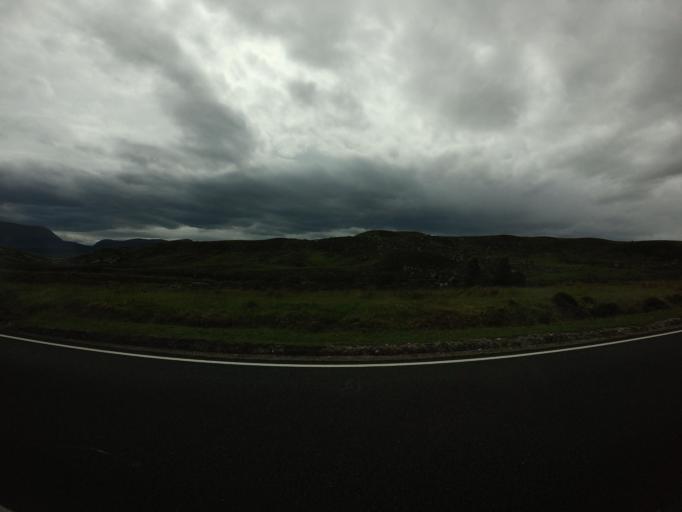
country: GB
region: Scotland
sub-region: Highland
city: Dingwall
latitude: 57.6977
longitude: -4.7296
